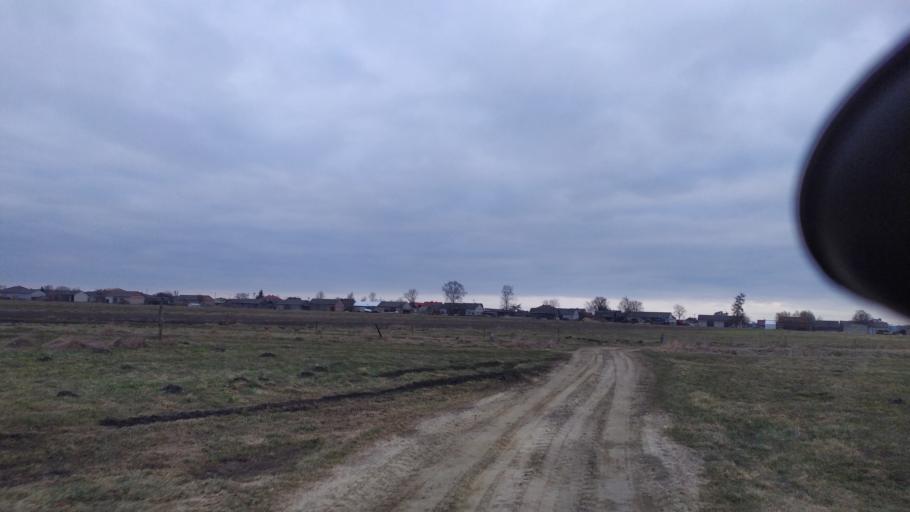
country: PL
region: Lublin Voivodeship
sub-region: Powiat lubartowski
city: Abramow
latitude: 51.4367
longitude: 22.2934
